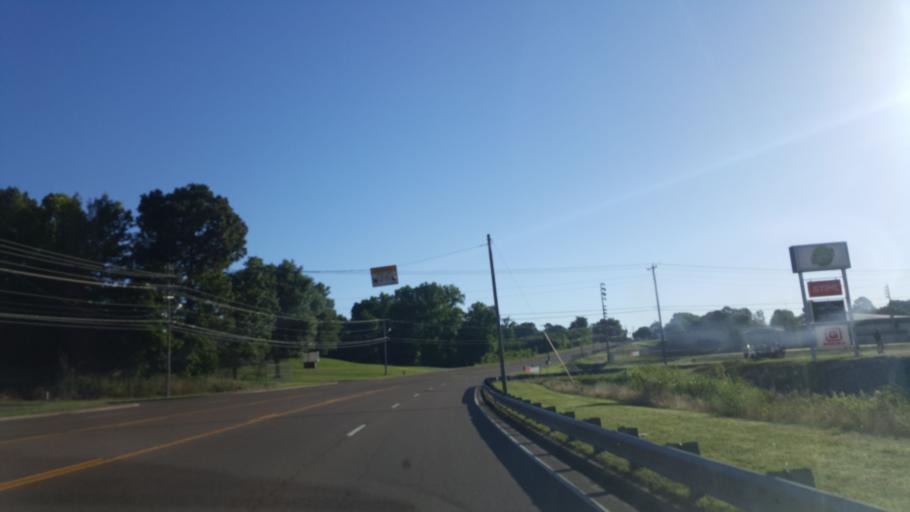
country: US
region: Tennessee
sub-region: Henderson County
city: Lexington
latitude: 35.6446
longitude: -88.4013
